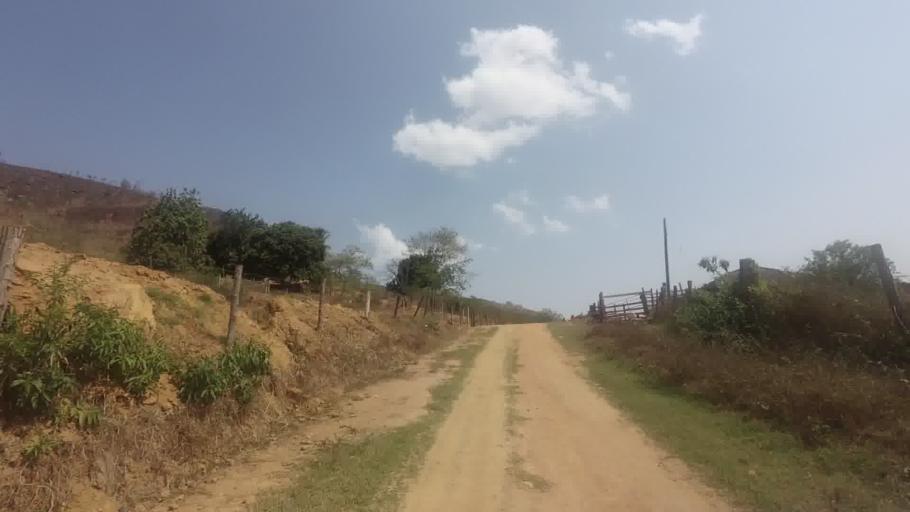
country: BR
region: Espirito Santo
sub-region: Sao Jose Do Calcado
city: Sao Jose do Calcado
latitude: -21.0303
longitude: -41.5175
